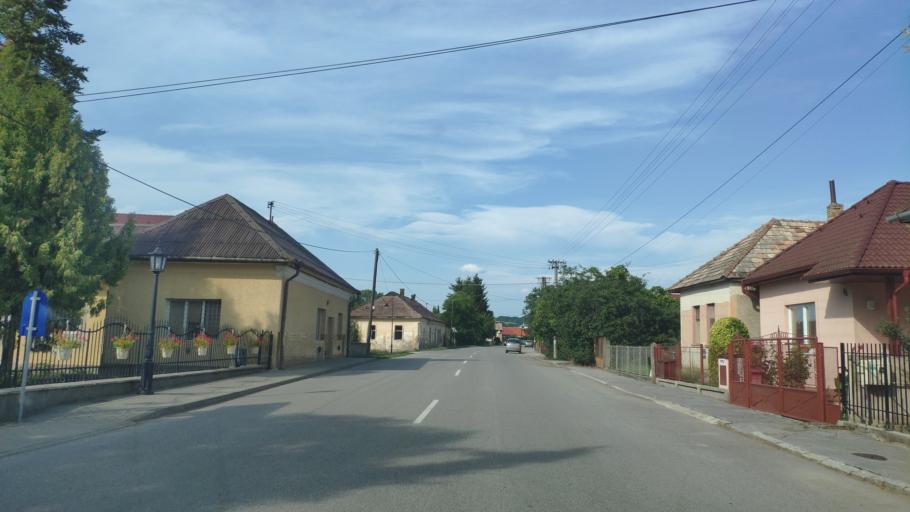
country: HU
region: Borsod-Abauj-Zemplen
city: Putnok
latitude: 48.4734
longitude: 20.3512
